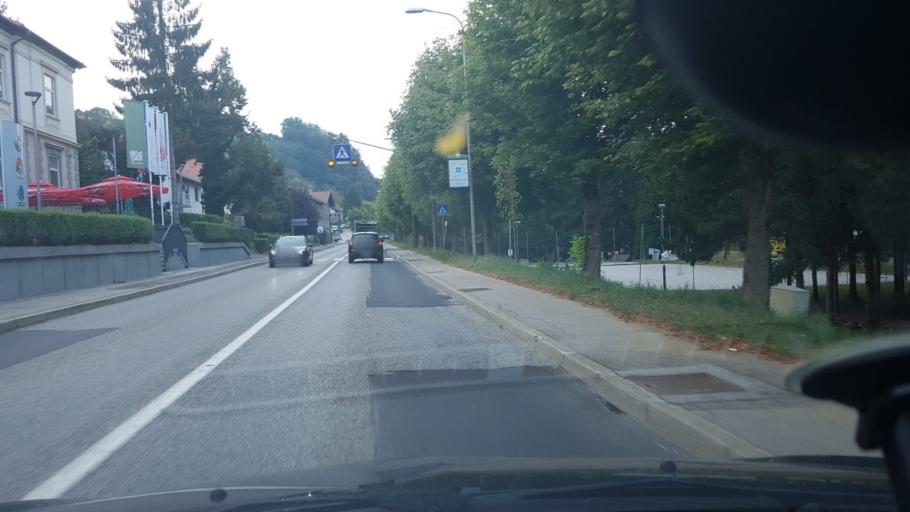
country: SI
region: Krsko
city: Krsko
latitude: 45.9518
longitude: 15.4868
